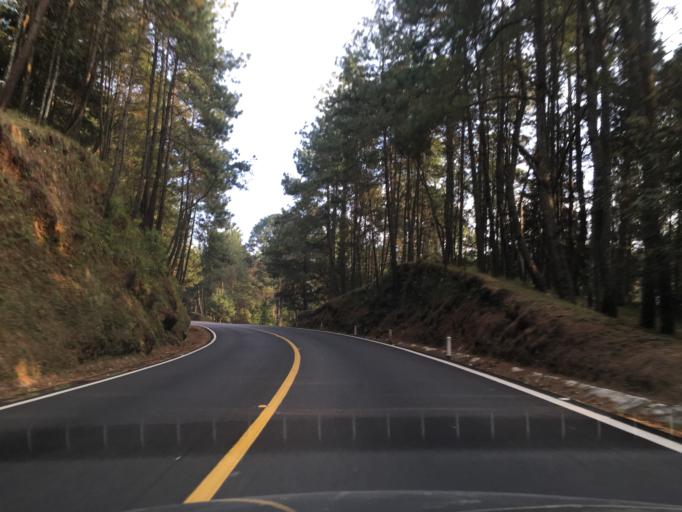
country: MX
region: Michoacan
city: Tingambato
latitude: 19.4942
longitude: -101.8229
